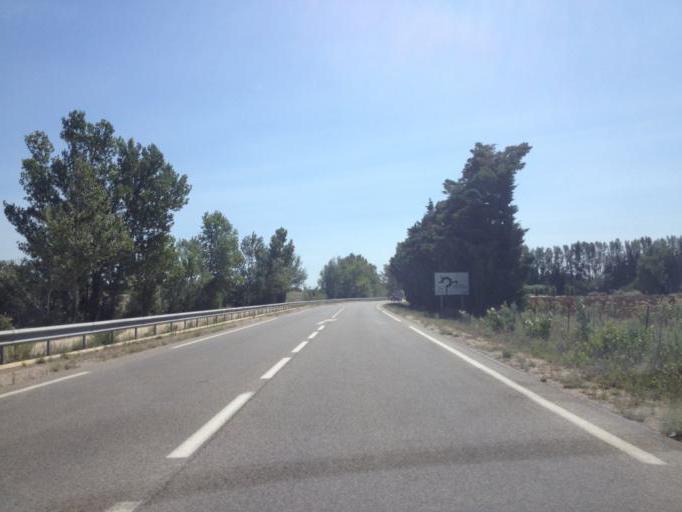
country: FR
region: Languedoc-Roussillon
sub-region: Departement du Gard
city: Roquemaure
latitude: 44.0462
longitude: 4.7922
